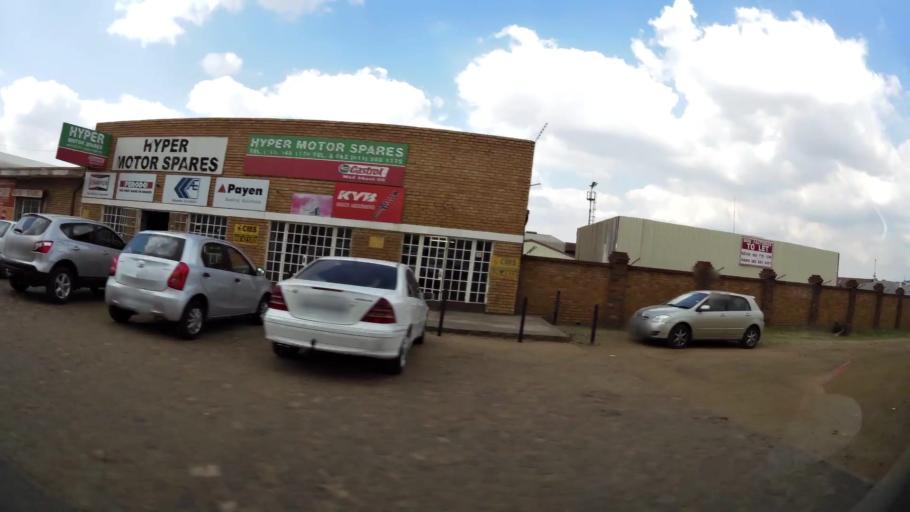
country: ZA
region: Gauteng
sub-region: Ekurhuleni Metropolitan Municipality
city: Benoni
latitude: -26.1279
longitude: 28.3551
